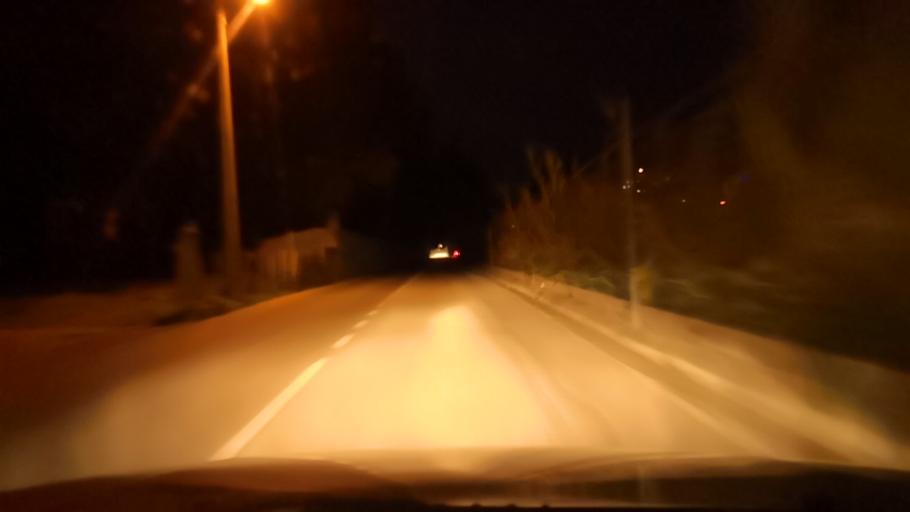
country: PT
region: Setubal
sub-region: Setubal
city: Setubal
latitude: 38.5413
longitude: -8.8892
